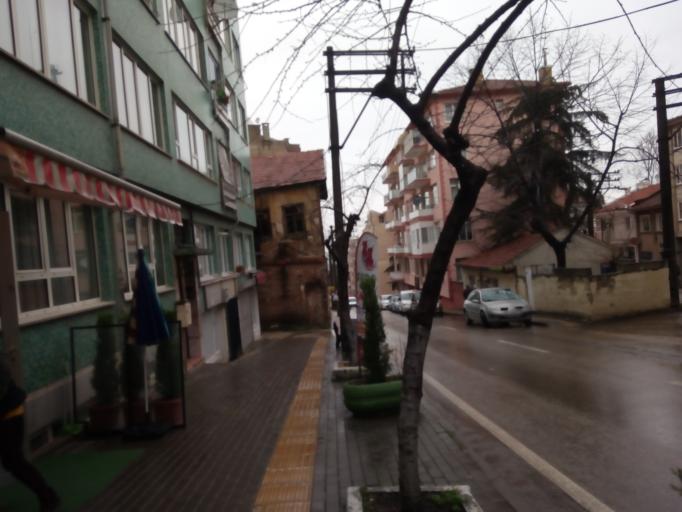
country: TR
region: Bursa
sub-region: Osmangazi
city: Bursa
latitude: 40.1782
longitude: 29.0620
